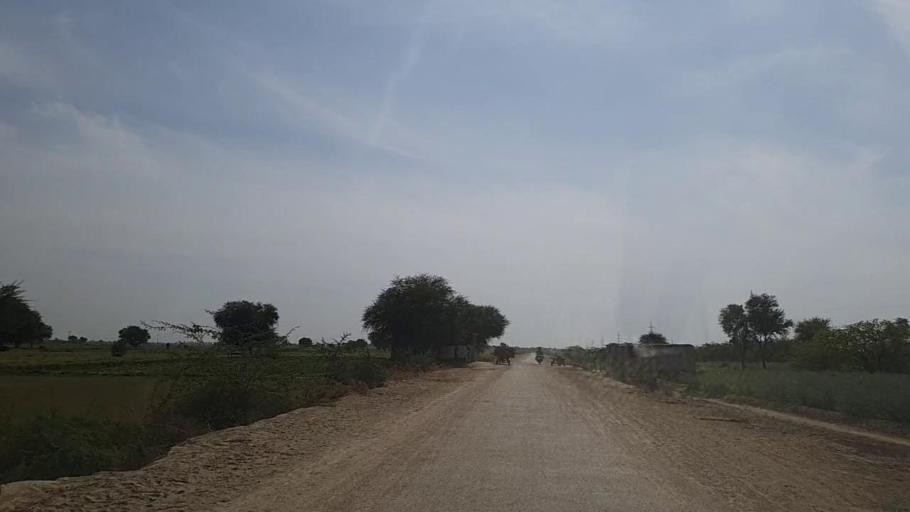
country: PK
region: Sindh
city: Kunri
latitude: 25.1801
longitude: 69.4580
